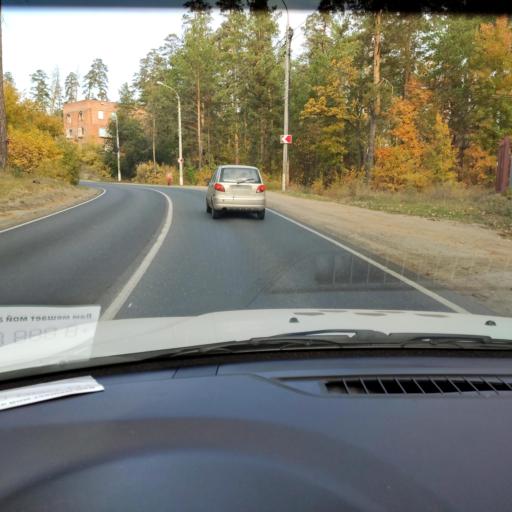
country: RU
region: Samara
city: Tol'yatti
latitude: 53.4879
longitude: 49.3110
